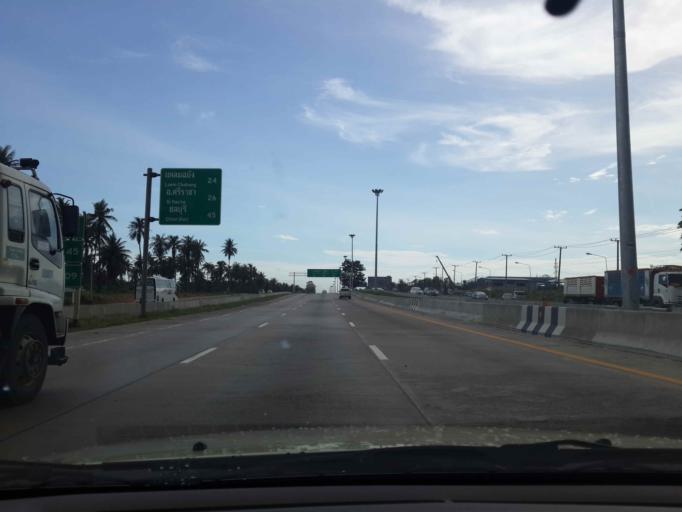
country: TH
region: Chon Buri
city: Bang Lamung
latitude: 12.9782
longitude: 100.9847
